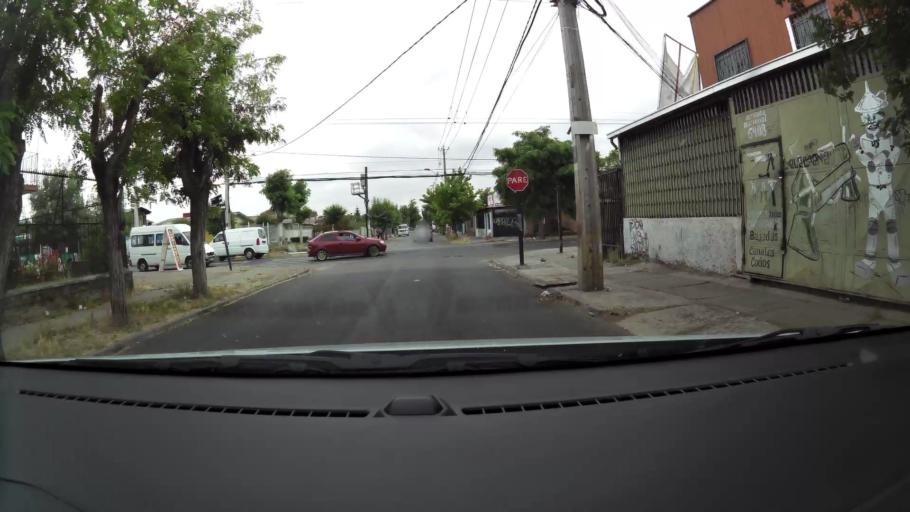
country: CL
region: Santiago Metropolitan
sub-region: Provincia de Santiago
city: Santiago
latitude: -33.5044
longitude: -70.6889
